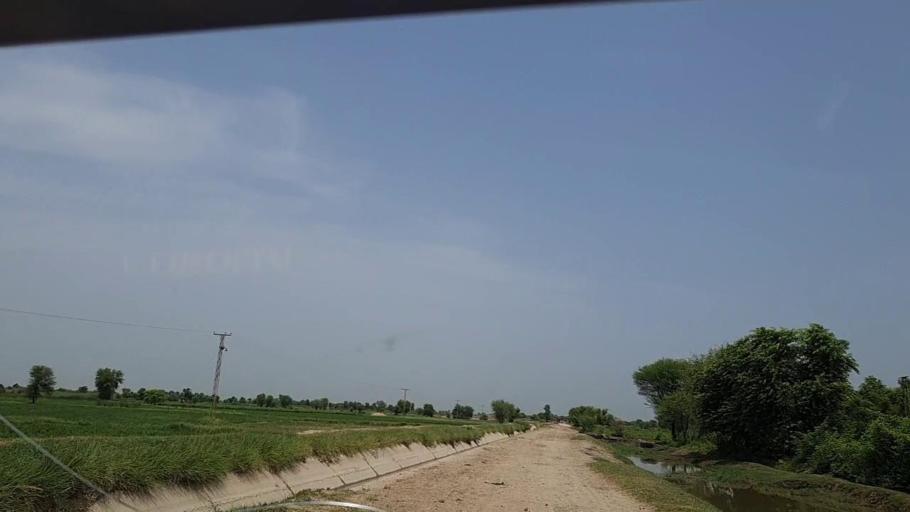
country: PK
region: Sindh
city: Tharu Shah
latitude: 26.9225
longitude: 68.0667
